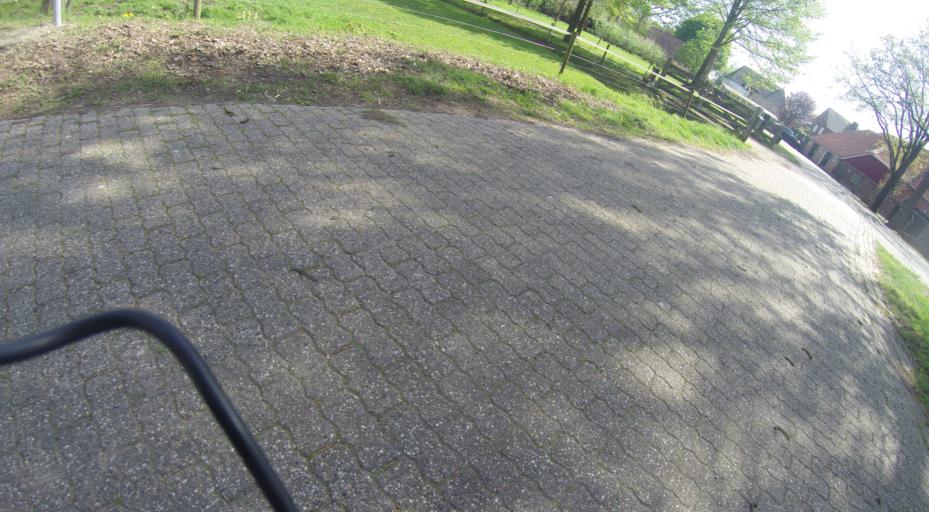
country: NL
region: Gelderland
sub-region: Oost Gelre
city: Lichtenvoorde
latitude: 52.0014
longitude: 6.5309
